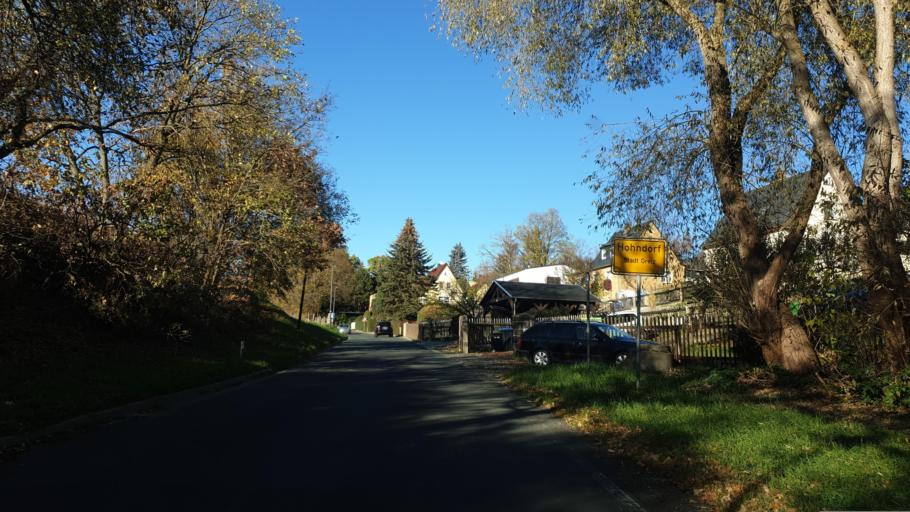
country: DE
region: Saxony
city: Elsterberg
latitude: 50.6101
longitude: 12.1403
